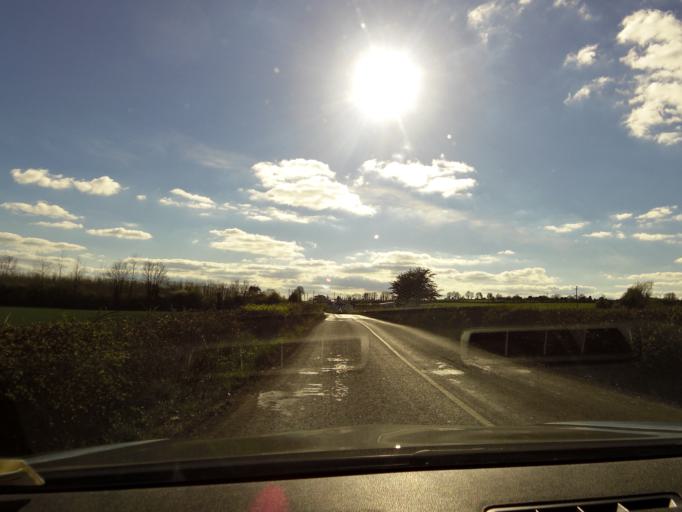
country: IE
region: Connaught
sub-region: County Galway
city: Portumna
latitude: 53.1073
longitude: -8.1279
